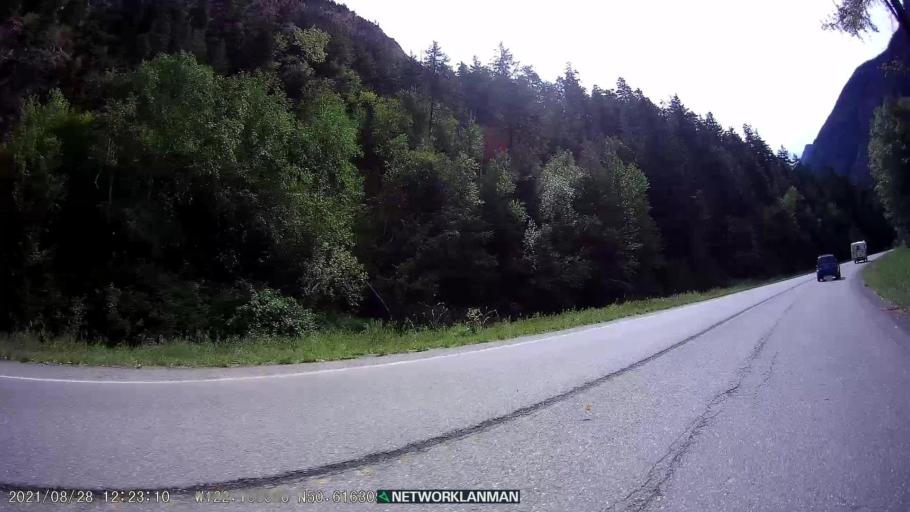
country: CA
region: British Columbia
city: Lillooet
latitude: 50.6161
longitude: -122.1032
